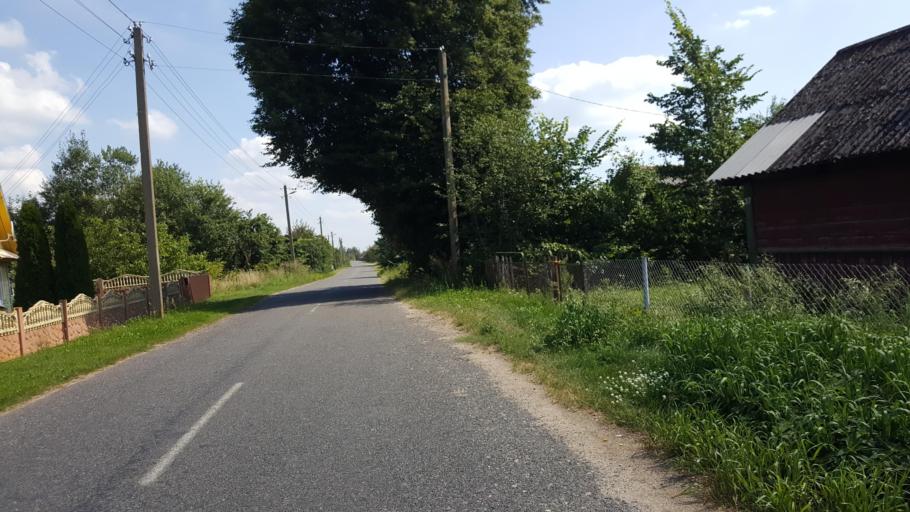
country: PL
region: Podlasie
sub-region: Powiat hajnowski
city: Czeremcha
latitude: 52.5129
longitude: 23.5449
